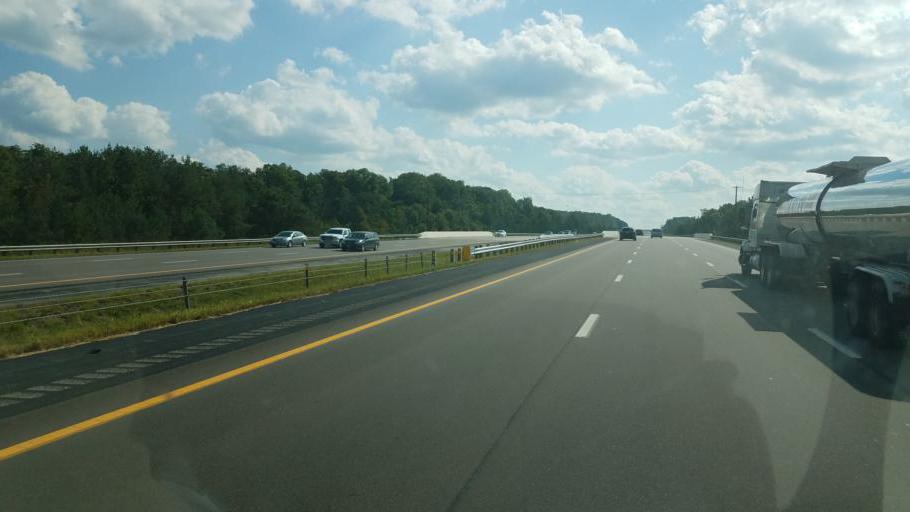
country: US
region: Ohio
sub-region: Medina County
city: Medina
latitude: 41.1080
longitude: -81.8157
